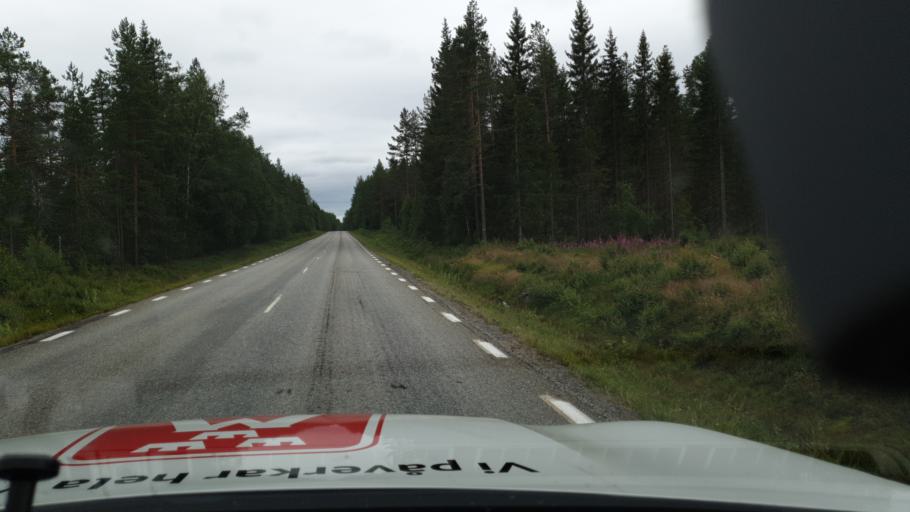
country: SE
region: Vaesterbotten
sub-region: Umea Kommun
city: Saevar
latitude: 64.0425
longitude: 20.4841
